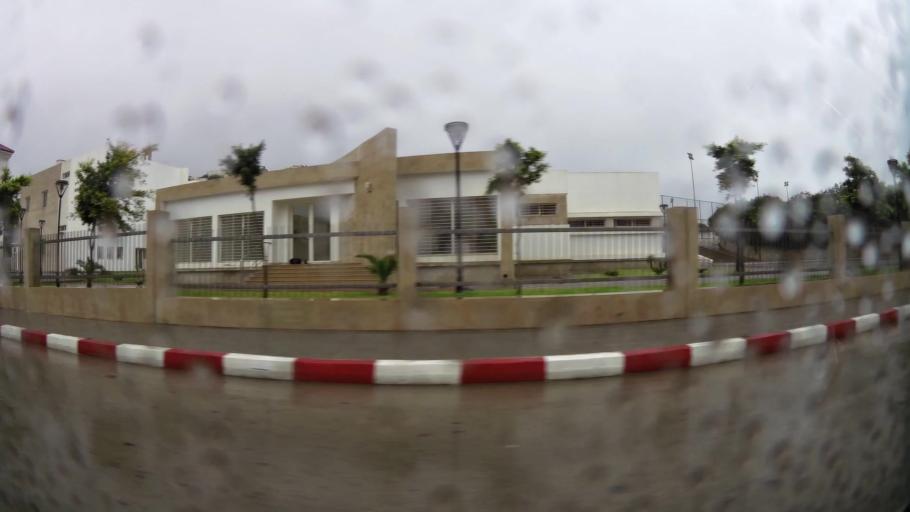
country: MA
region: Taza-Al Hoceima-Taounate
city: Al Hoceima
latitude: 35.2487
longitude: -3.9423
